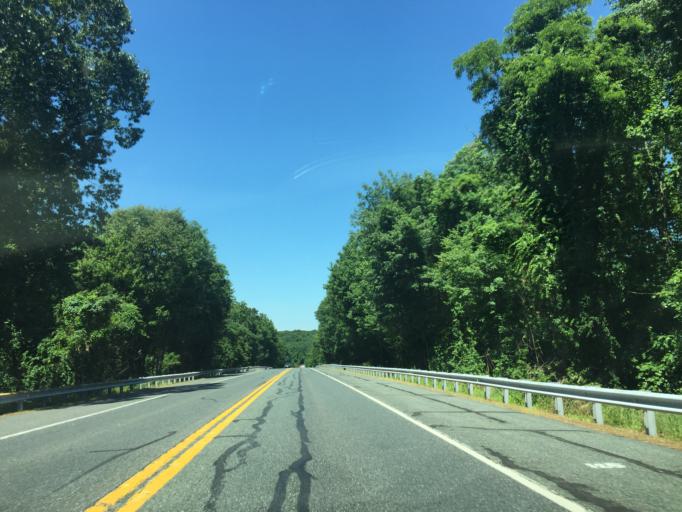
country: US
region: Maryland
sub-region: Harford County
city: Jarrettsville
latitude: 39.5754
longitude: -76.4304
